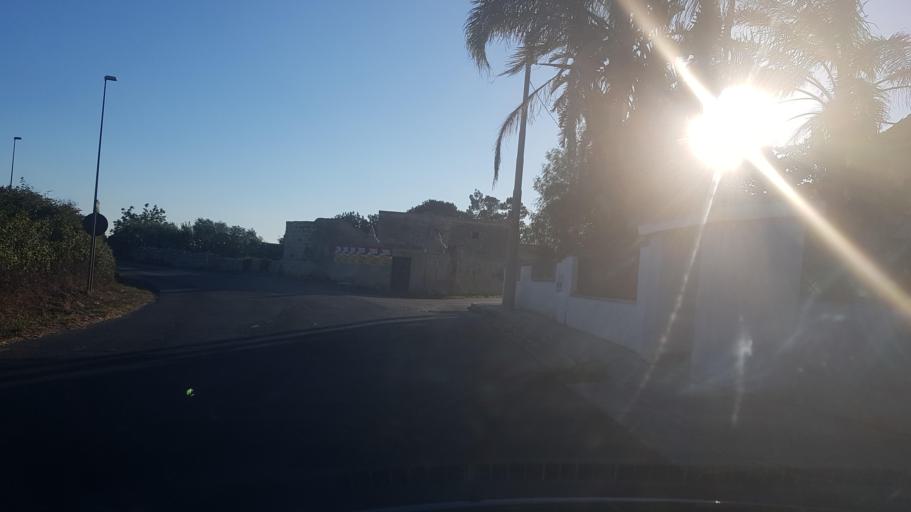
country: IT
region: Apulia
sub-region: Provincia di Lecce
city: Struda
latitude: 40.3329
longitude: 18.2945
